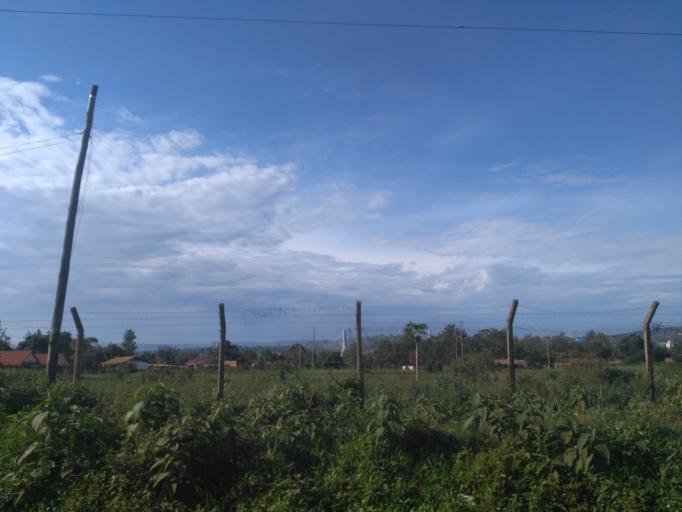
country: UG
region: Eastern Region
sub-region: Jinja District
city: Jinja
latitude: 0.4499
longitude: 33.1943
